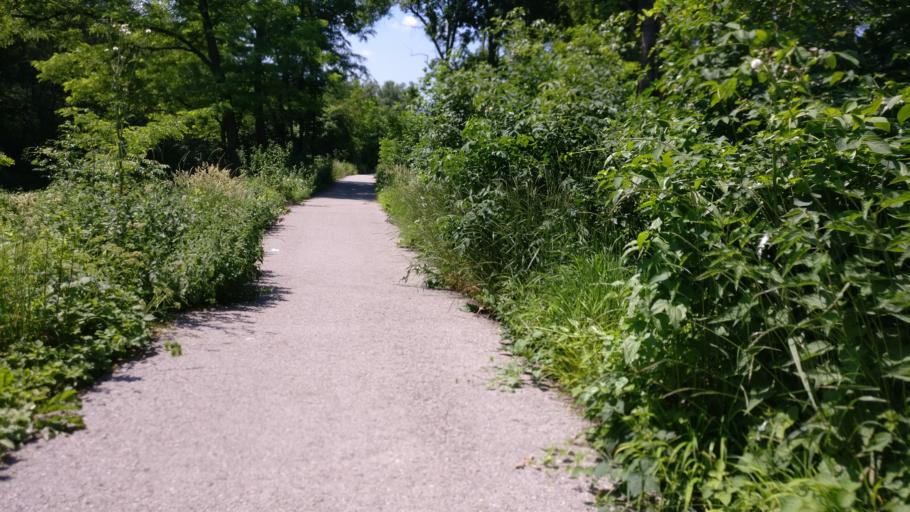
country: AT
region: Lower Austria
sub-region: Politischer Bezirk Baden
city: Oberwaltersdorf
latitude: 47.9688
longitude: 16.3138
